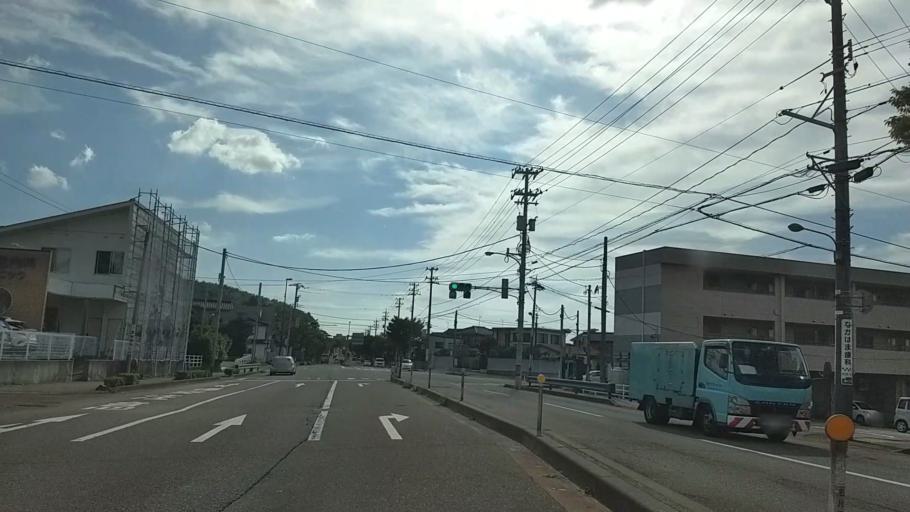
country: JP
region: Ishikawa
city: Nonoichi
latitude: 36.5237
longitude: 136.6419
